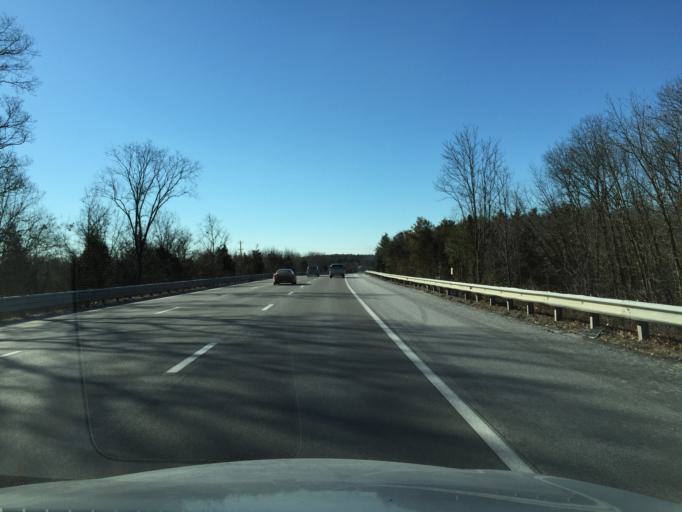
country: US
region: Massachusetts
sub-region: Bristol County
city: Mansfield
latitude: 42.0332
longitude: -71.2499
